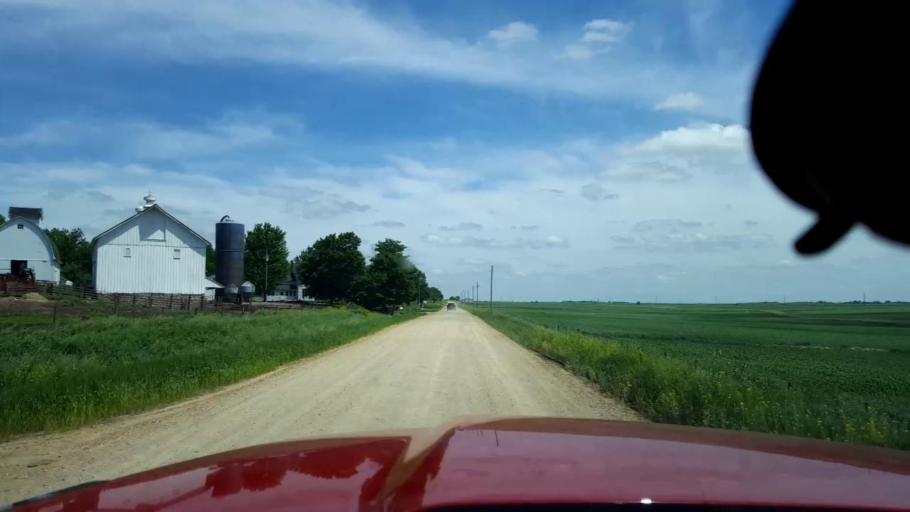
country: US
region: Iowa
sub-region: Linn County
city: Lisbon
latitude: 41.9543
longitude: -91.3605
